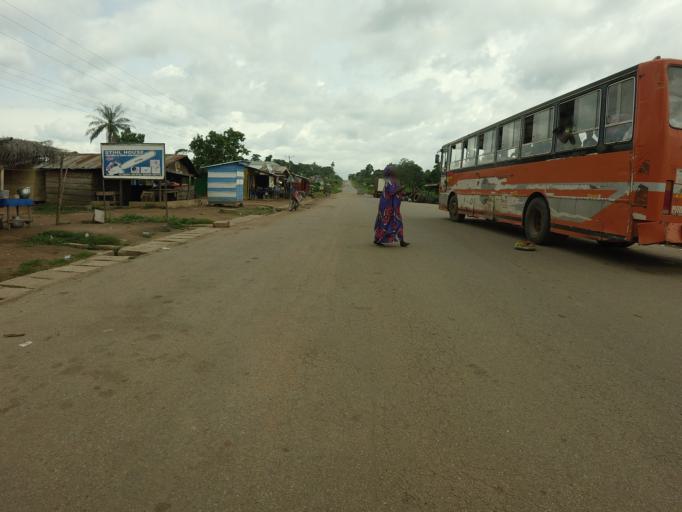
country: TG
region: Plateaux
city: Badou
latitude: 7.8227
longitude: 0.5330
